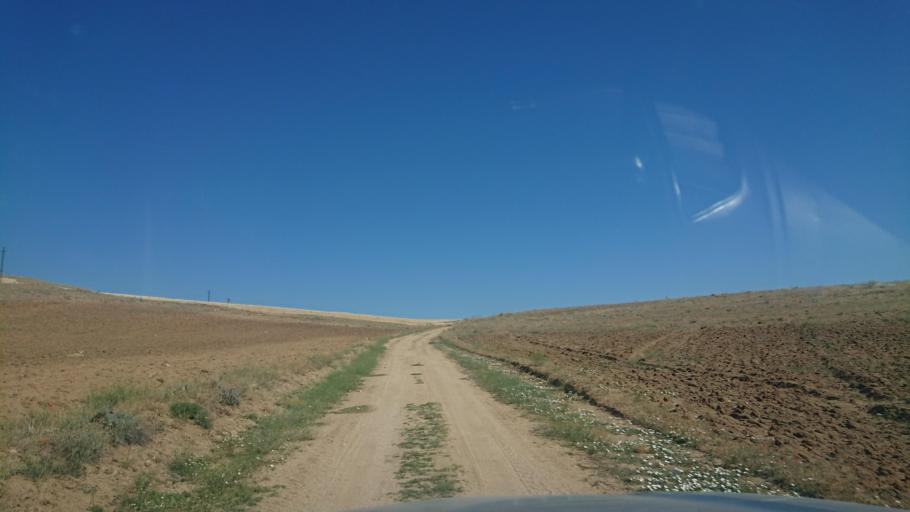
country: TR
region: Aksaray
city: Agacoren
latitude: 38.9107
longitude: 33.8974
